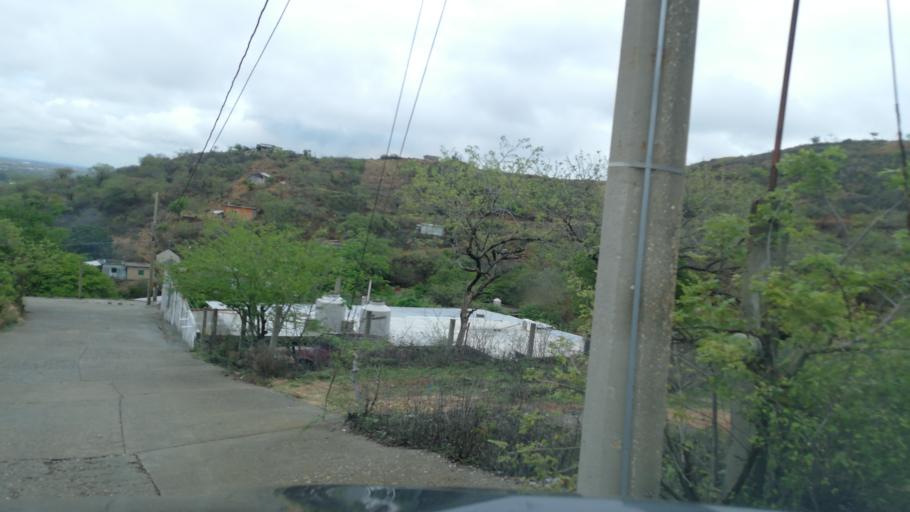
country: MX
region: Oaxaca
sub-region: Salina Cruz
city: Salina Cruz
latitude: 16.1811
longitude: -95.1839
